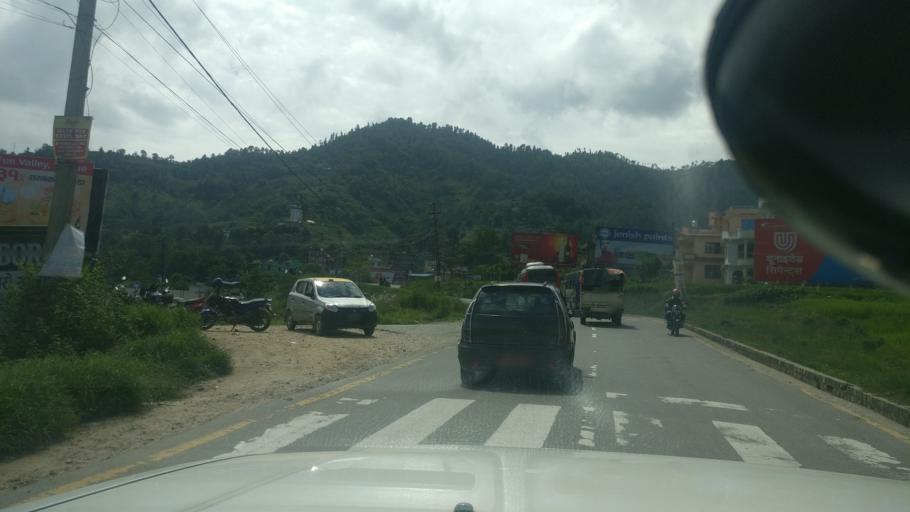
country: NP
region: Central Region
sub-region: Bagmati Zone
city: kankrabari Dovan
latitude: 27.6476
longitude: 85.4653
